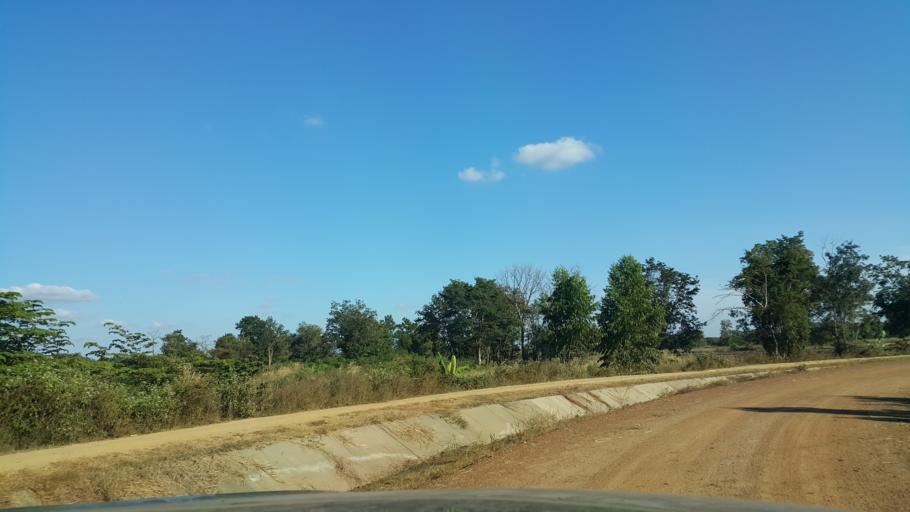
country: TH
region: Sukhothai
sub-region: Amphoe Si Satchanalai
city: Si Satchanalai
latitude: 17.4720
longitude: 99.6622
